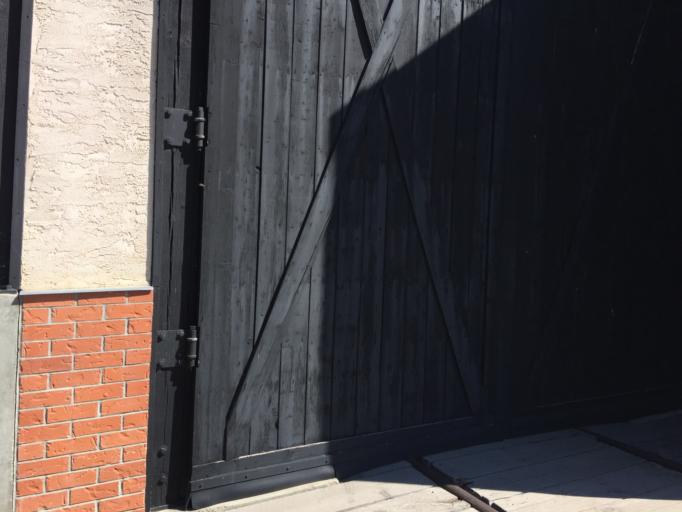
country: CA
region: Alberta
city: Calgary
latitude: 50.9863
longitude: -114.1091
